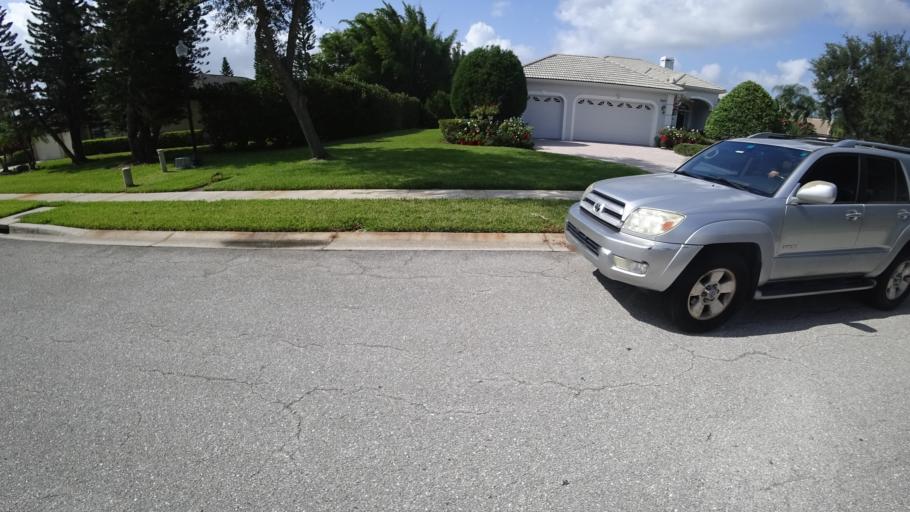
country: US
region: Florida
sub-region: Sarasota County
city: The Meadows
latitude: 27.4050
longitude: -82.4338
